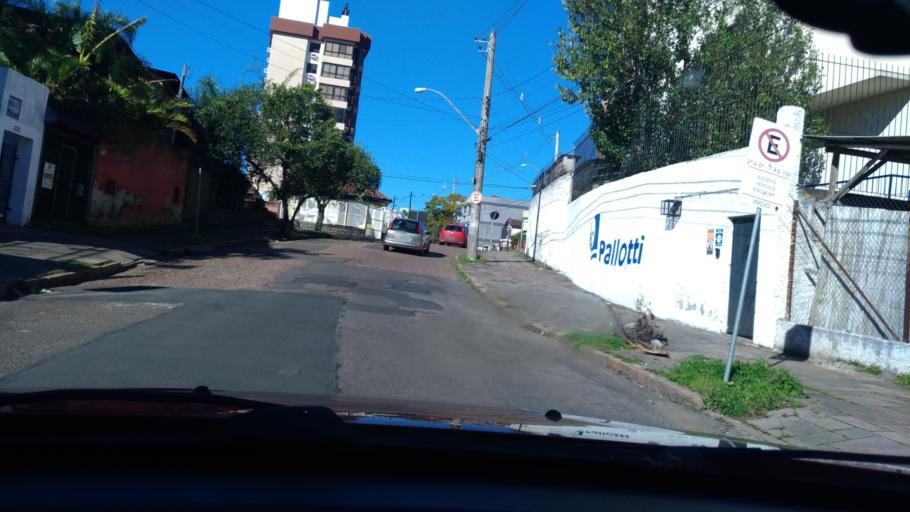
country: BR
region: Rio Grande do Sul
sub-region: Porto Alegre
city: Porto Alegre
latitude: -30.0098
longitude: -51.1701
